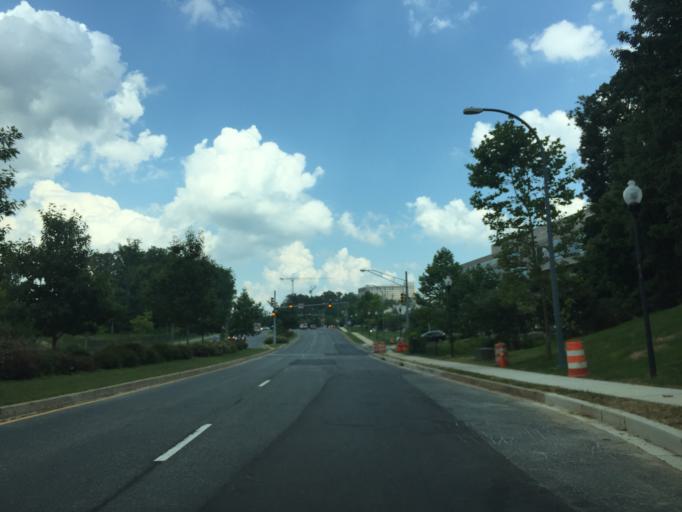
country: US
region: Maryland
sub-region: Montgomery County
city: North Bethesda
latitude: 39.0511
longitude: -77.1288
